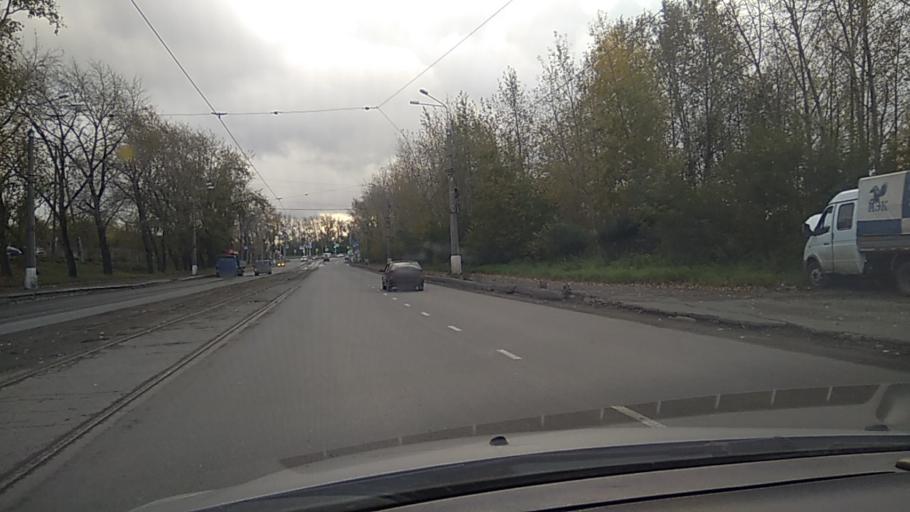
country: RU
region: Sverdlovsk
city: Nizhniy Tagil
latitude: 57.9242
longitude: 59.9901
